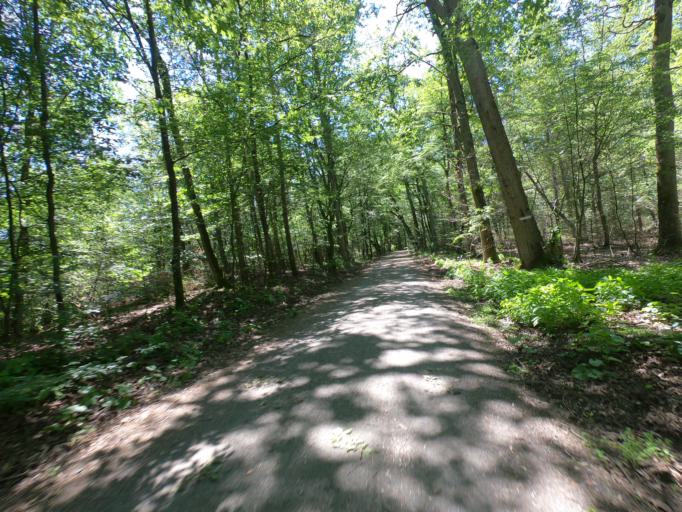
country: DE
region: Hesse
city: Niederrad
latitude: 50.0456
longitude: 8.6452
